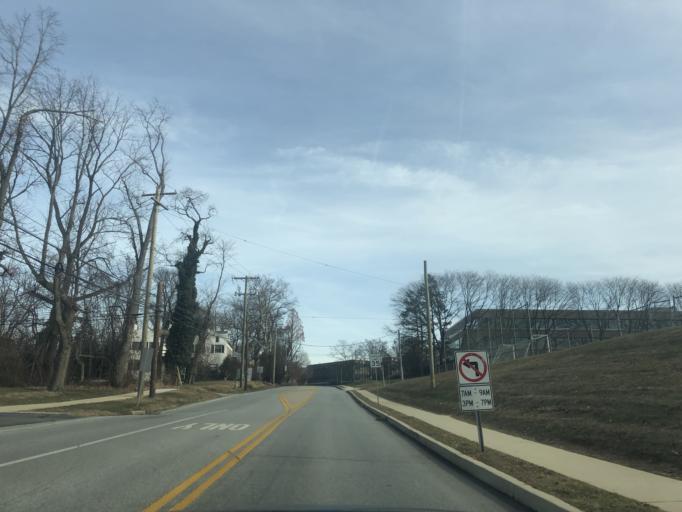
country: US
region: Pennsylvania
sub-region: Delaware County
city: Radnor
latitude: 40.0416
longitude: -75.3622
